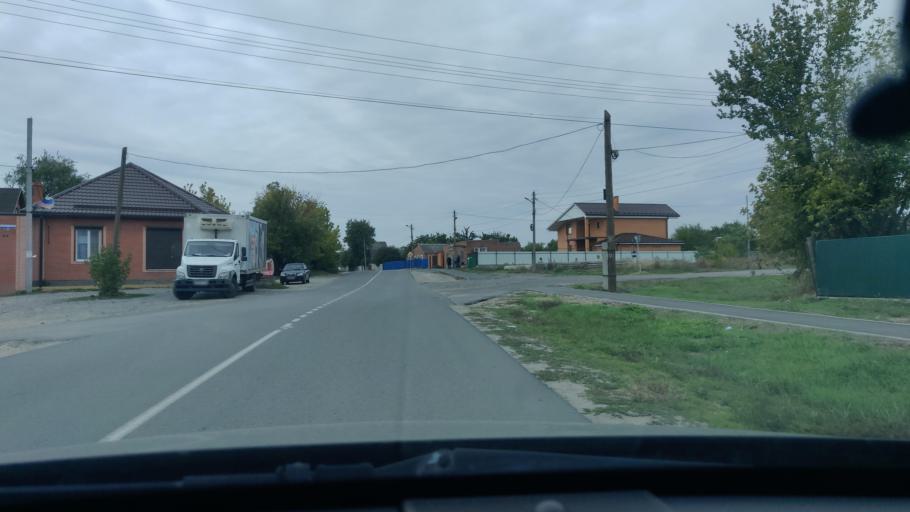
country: RU
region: Rostov
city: Ust'-Donetskiy
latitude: 47.6585
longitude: 40.9140
